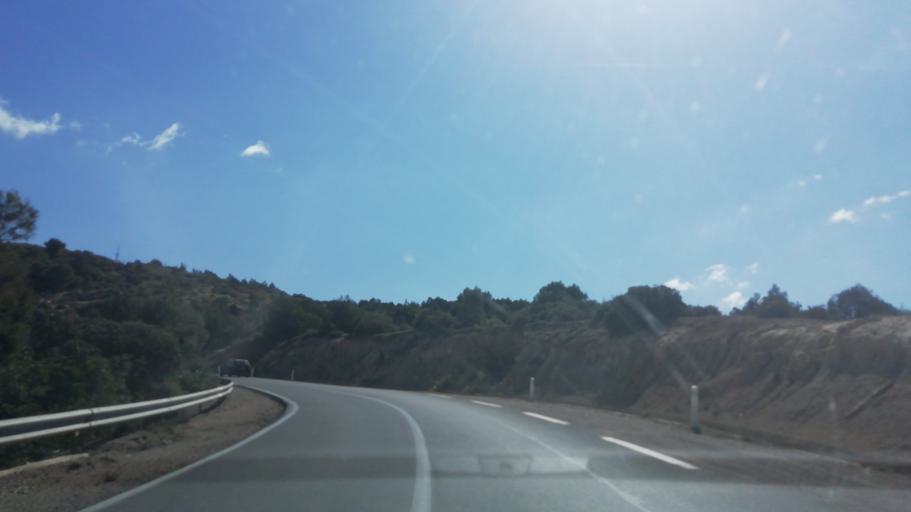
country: DZ
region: Mascara
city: Mascara
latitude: 35.4841
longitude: 0.1520
